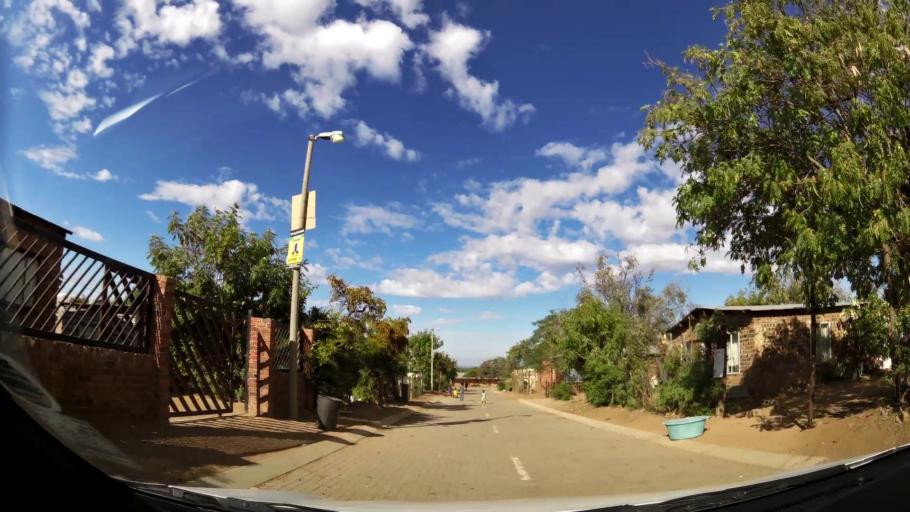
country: ZA
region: Limpopo
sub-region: Waterberg District Municipality
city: Warmbaths
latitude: -24.8757
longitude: 28.2716
